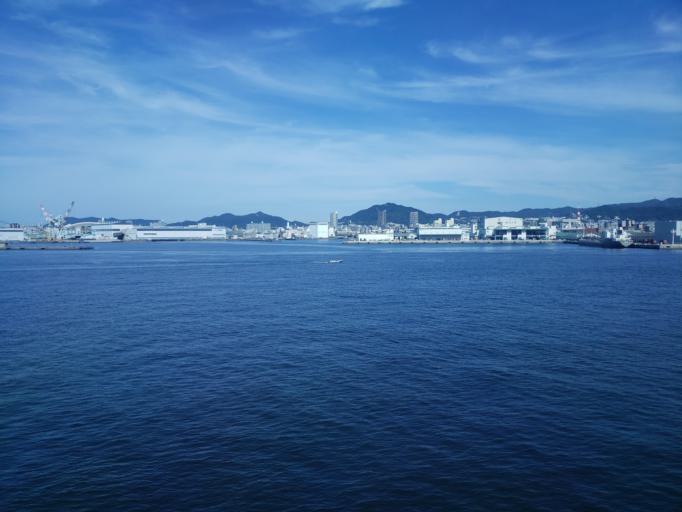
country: JP
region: Hyogo
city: Kobe
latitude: 34.6603
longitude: 135.1897
